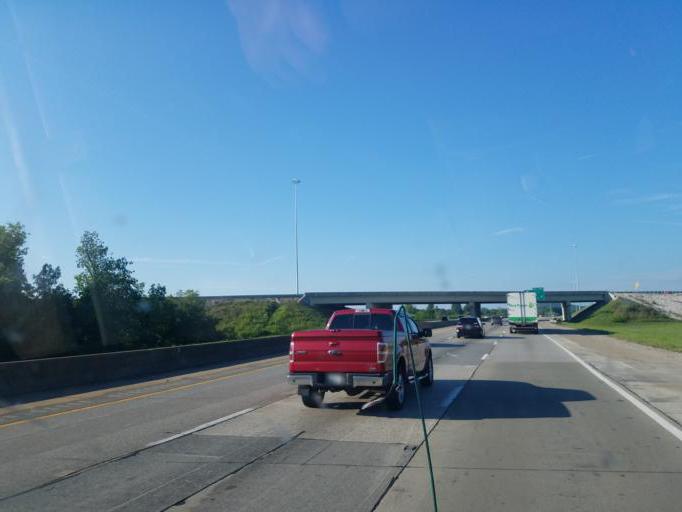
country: US
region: Kentucky
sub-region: Bullitt County
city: Lebanon Junction
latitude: 37.8028
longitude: -85.7484
